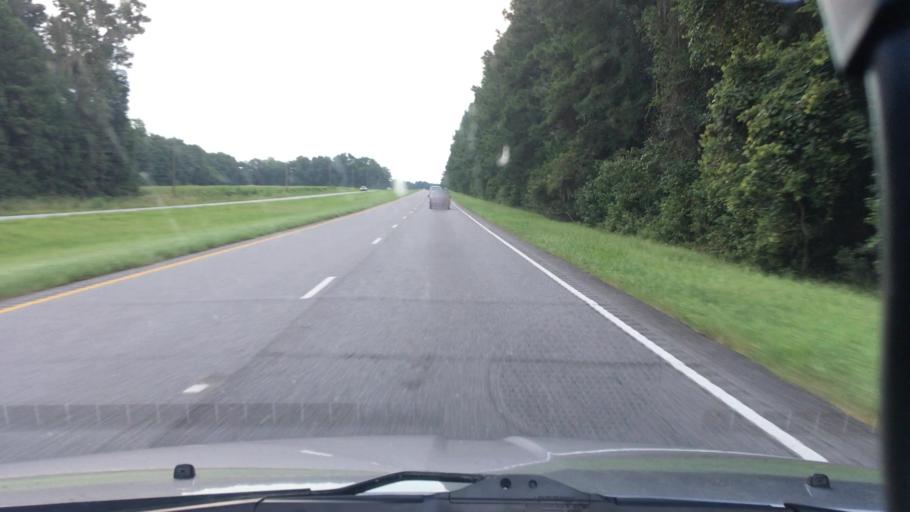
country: US
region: South Carolina
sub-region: Hampton County
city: Yemassee
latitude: 32.6168
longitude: -80.8178
